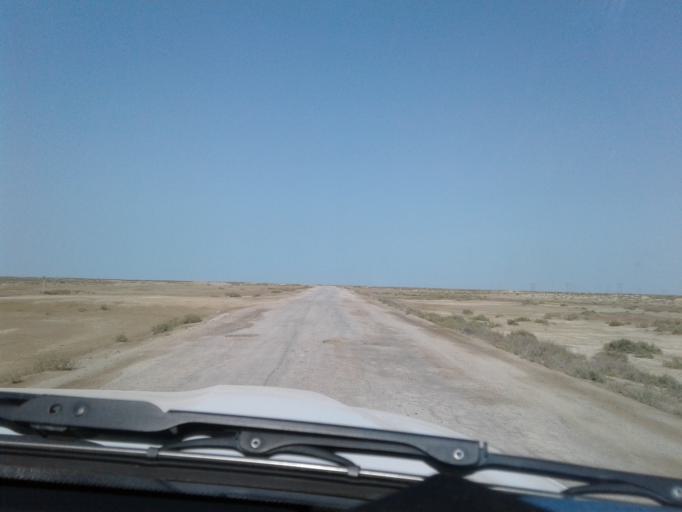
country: IR
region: Golestan
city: Gomishan
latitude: 37.8364
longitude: 53.9037
